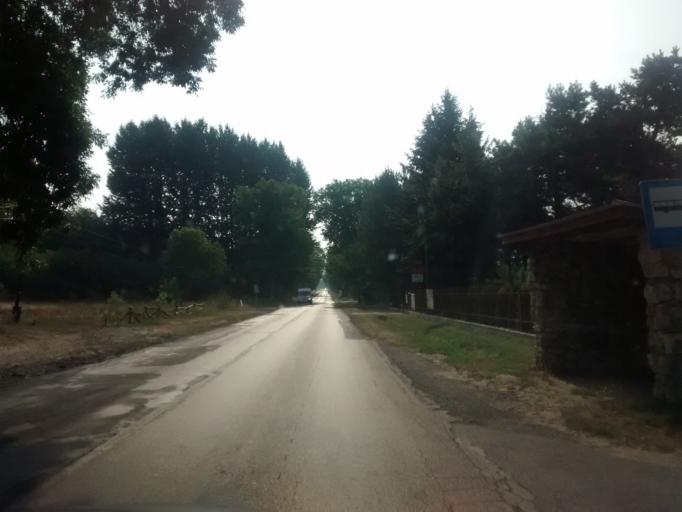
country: PL
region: Silesian Voivodeship
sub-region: Powiat zawiercianski
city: Kroczyce
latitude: 50.5669
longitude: 19.5356
